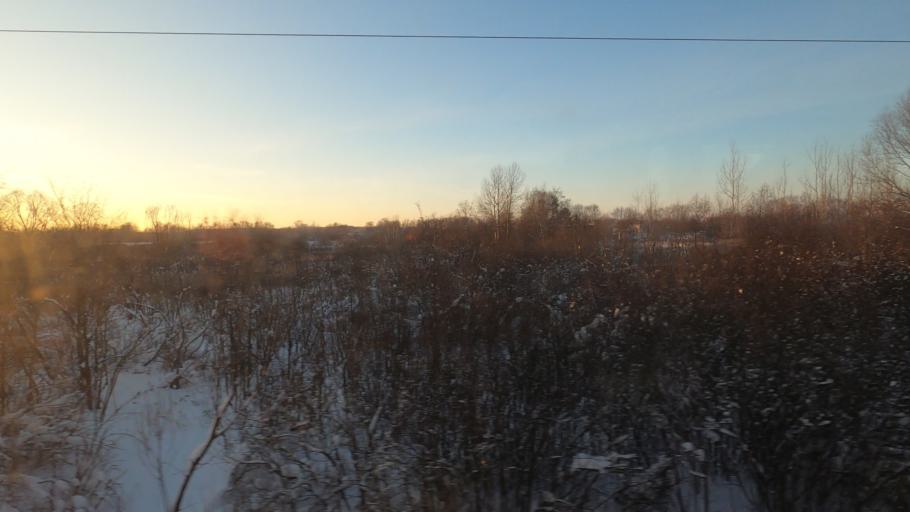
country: RU
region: Moskovskaya
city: Dmitrov
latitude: 56.3612
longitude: 37.5227
